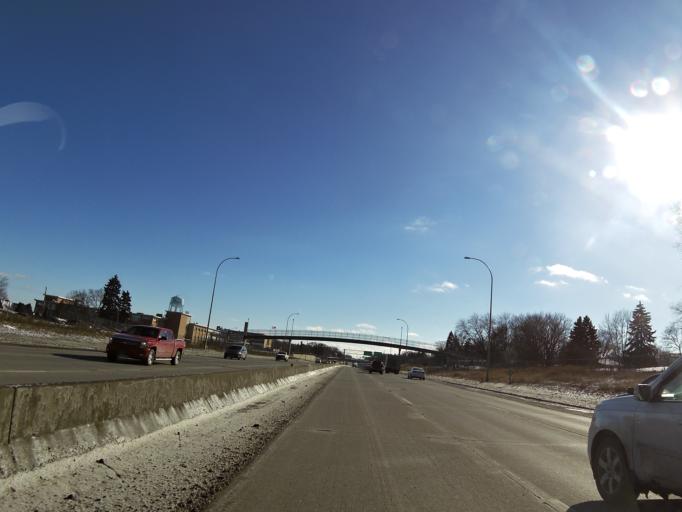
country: US
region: Minnesota
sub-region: Hennepin County
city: Edina
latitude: 44.9018
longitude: -93.3500
